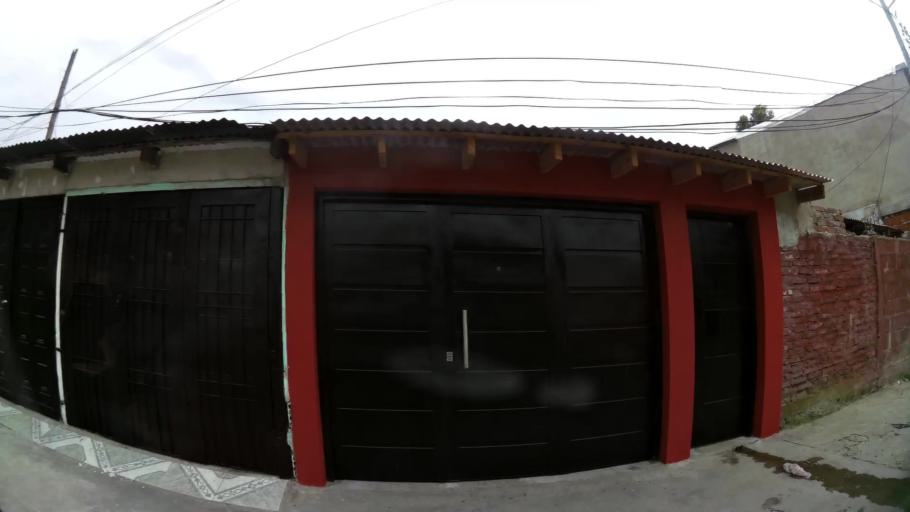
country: AR
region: Buenos Aires
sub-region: Partido de Avellaneda
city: Avellaneda
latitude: -34.6537
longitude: -58.3616
